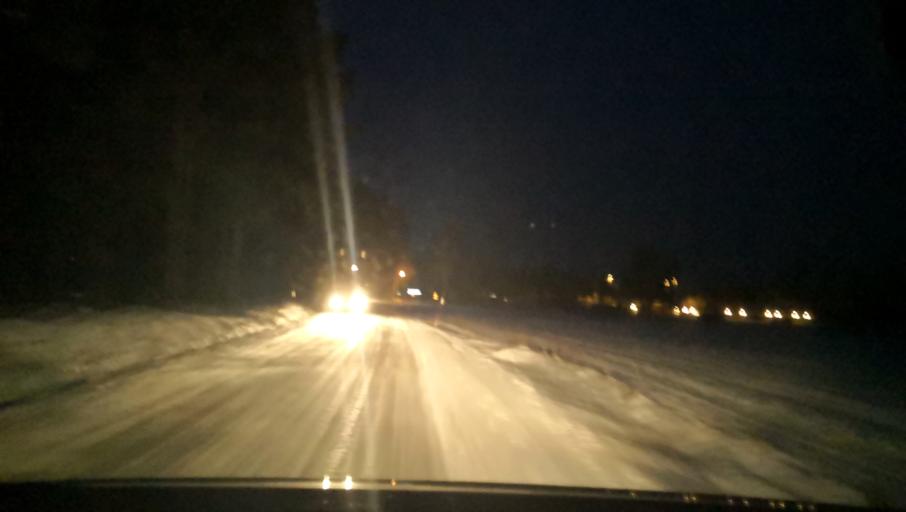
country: SE
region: Uppsala
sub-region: Heby Kommun
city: Tarnsjo
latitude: 60.2973
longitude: 16.8055
